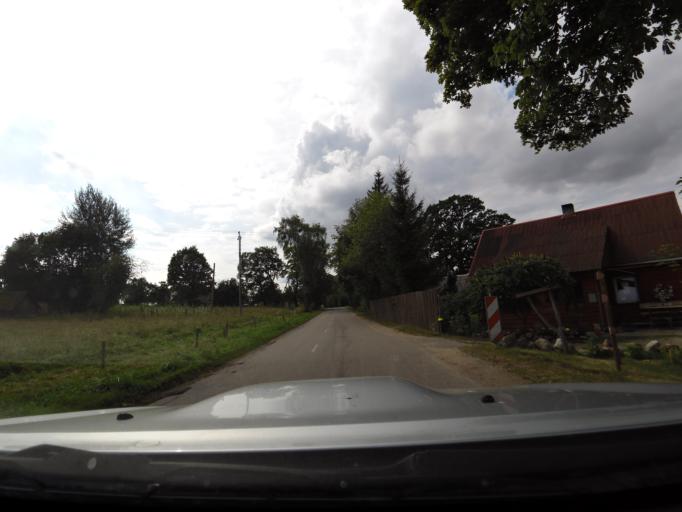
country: LT
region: Vilnius County
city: Elektrenai
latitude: 54.9026
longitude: 24.7225
